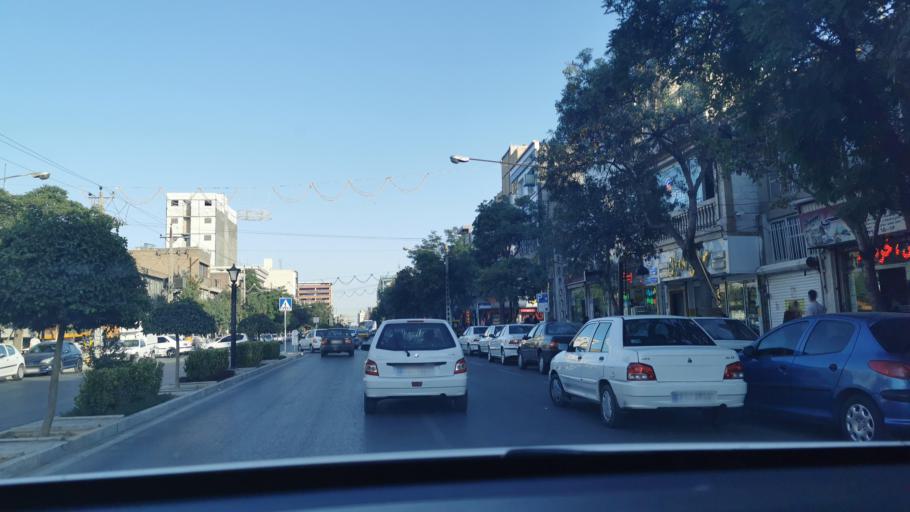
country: IR
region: Razavi Khorasan
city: Mashhad
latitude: 36.2953
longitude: 59.6441
